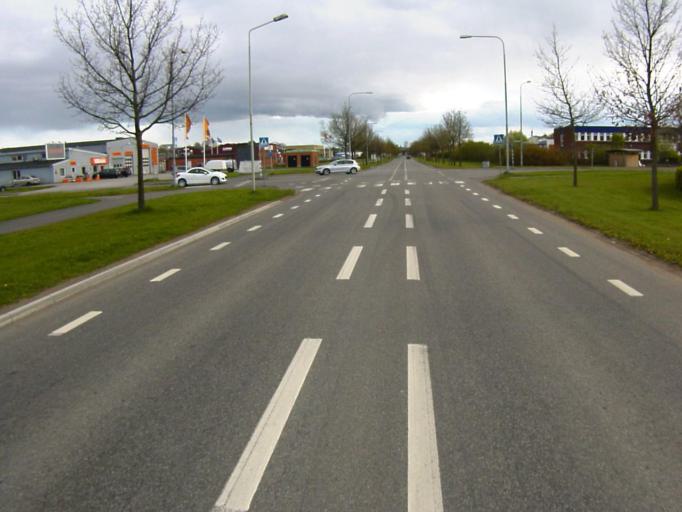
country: SE
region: Skane
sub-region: Kristianstads Kommun
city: Kristianstad
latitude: 56.0495
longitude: 14.1623
